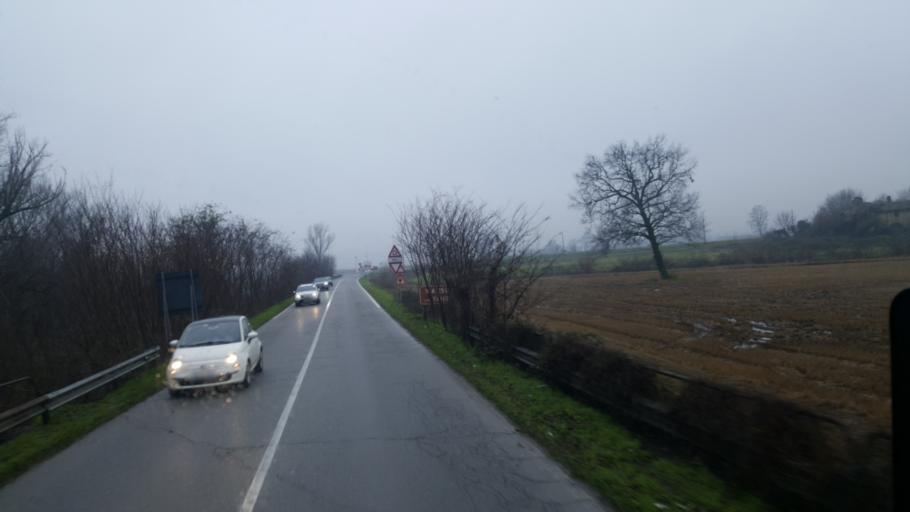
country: IT
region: Lombardy
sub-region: Provincia di Pavia
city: Lardirago
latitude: 45.2334
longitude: 9.2270
